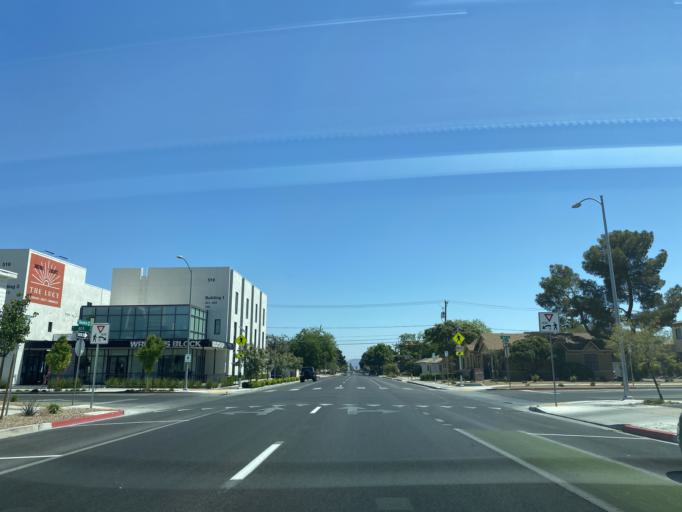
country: US
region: Nevada
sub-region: Clark County
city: Las Vegas
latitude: 36.1630
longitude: -115.1437
